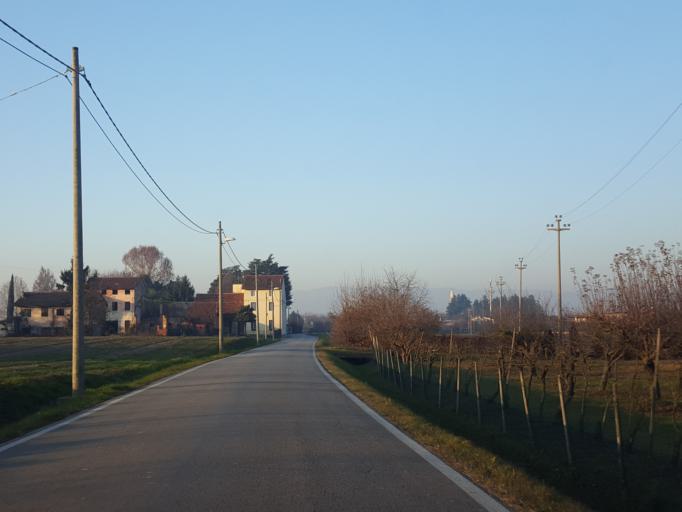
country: IT
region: Veneto
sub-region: Provincia di Vicenza
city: Villaggio Montegrappa
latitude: 45.5500
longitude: 11.6042
